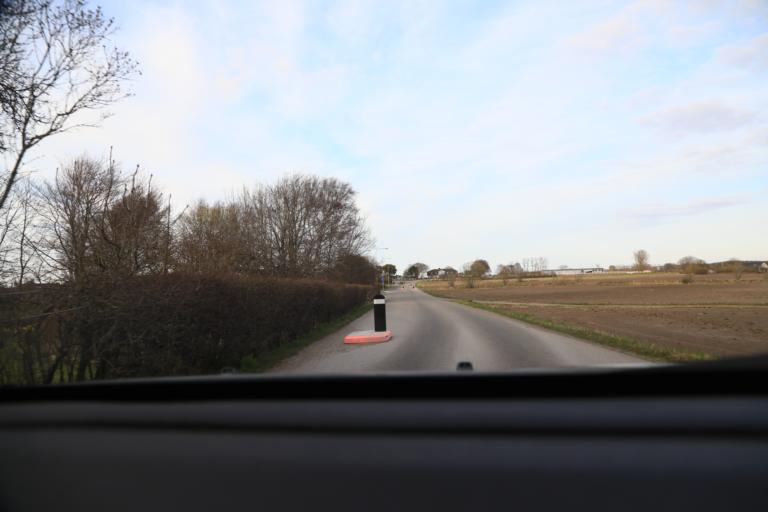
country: SE
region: Halland
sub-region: Varbergs Kommun
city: Traslovslage
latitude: 57.0759
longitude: 12.2753
